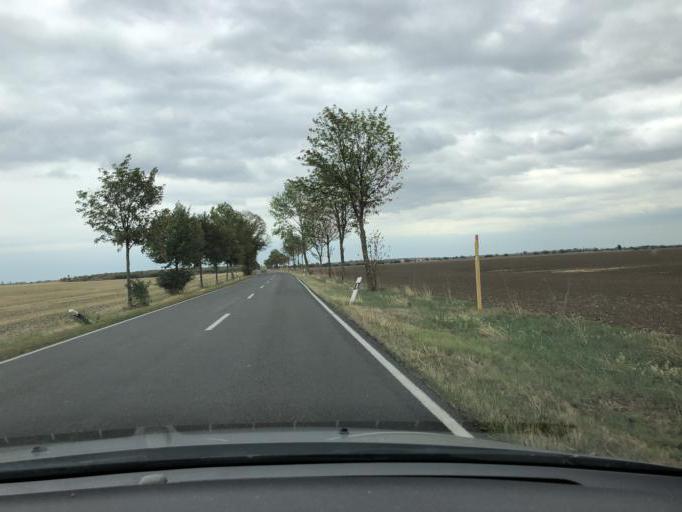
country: DE
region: Saxony-Anhalt
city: Nienburg/Saale
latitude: 51.8453
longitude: 11.7272
